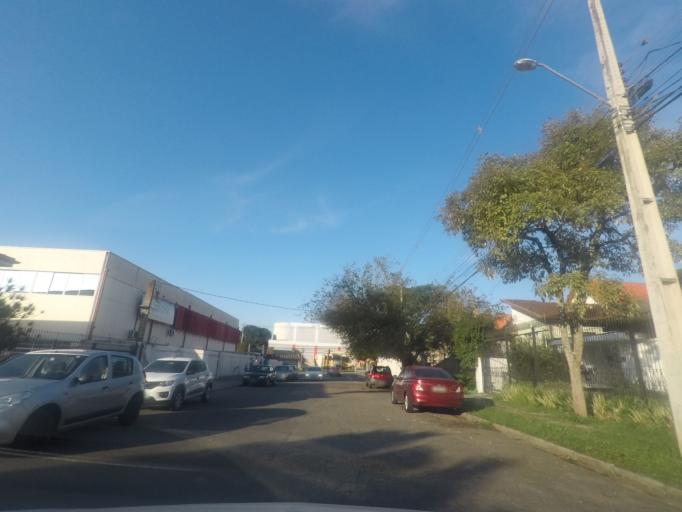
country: BR
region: Parana
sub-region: Curitiba
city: Curitiba
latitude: -25.4102
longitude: -49.2730
